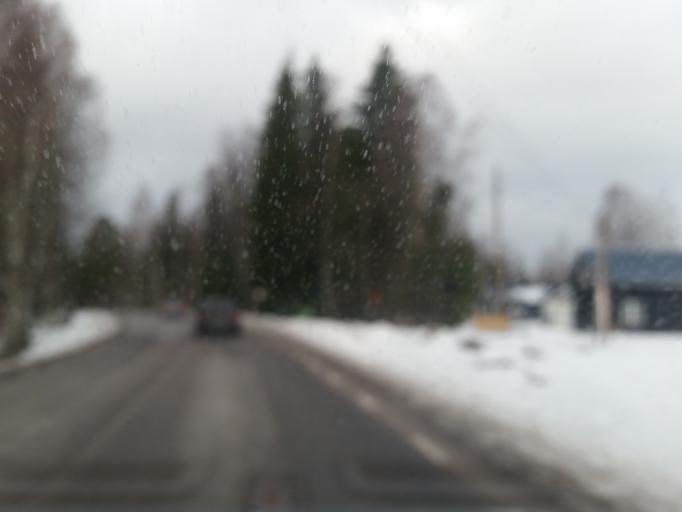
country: SE
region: Gaevleborg
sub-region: Sandvikens Kommun
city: Jarbo
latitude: 60.7632
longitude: 16.5131
